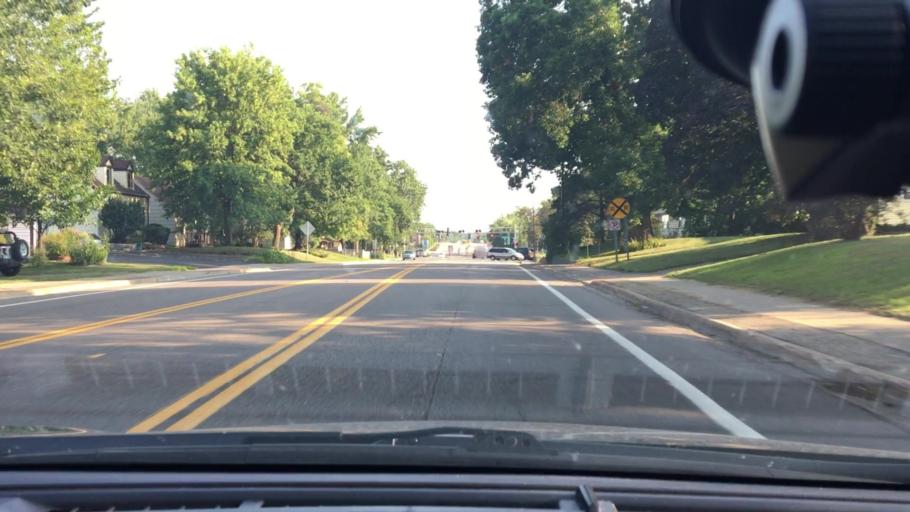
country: US
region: Minnesota
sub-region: Hennepin County
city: Golden Valley
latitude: 44.9911
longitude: -93.3805
